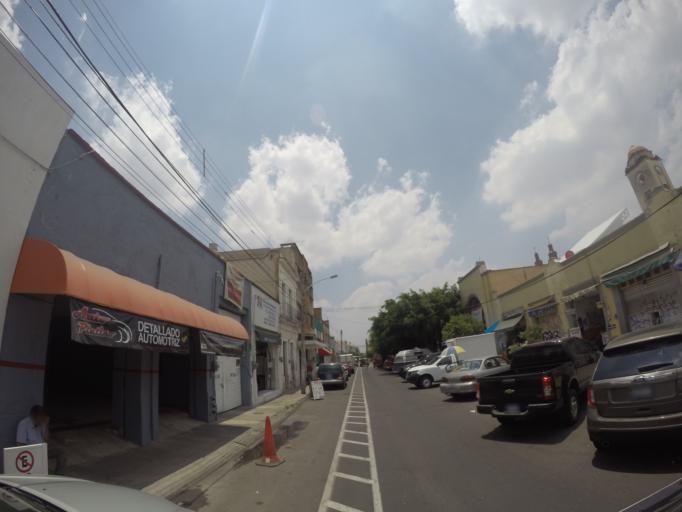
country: MX
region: Jalisco
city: Guadalajara
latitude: 20.6819
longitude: -103.3572
